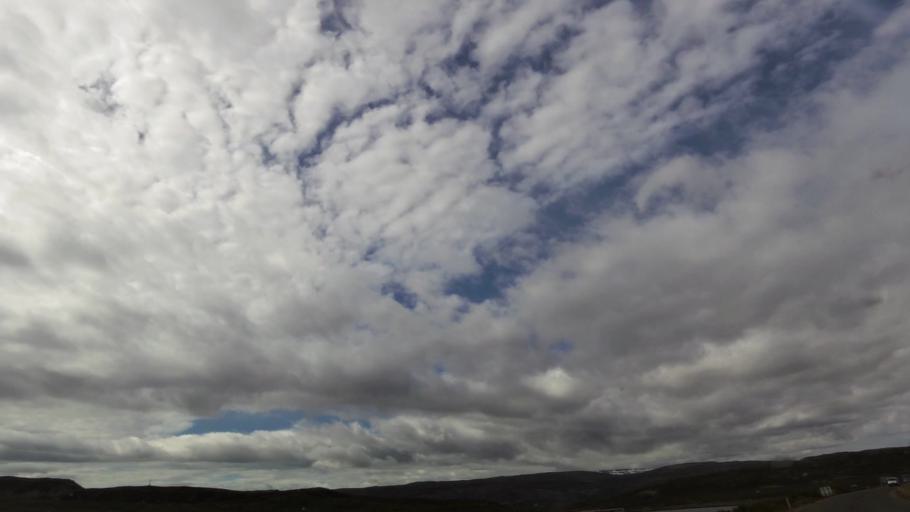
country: IS
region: West
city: Stykkisholmur
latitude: 65.5478
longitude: -22.0991
